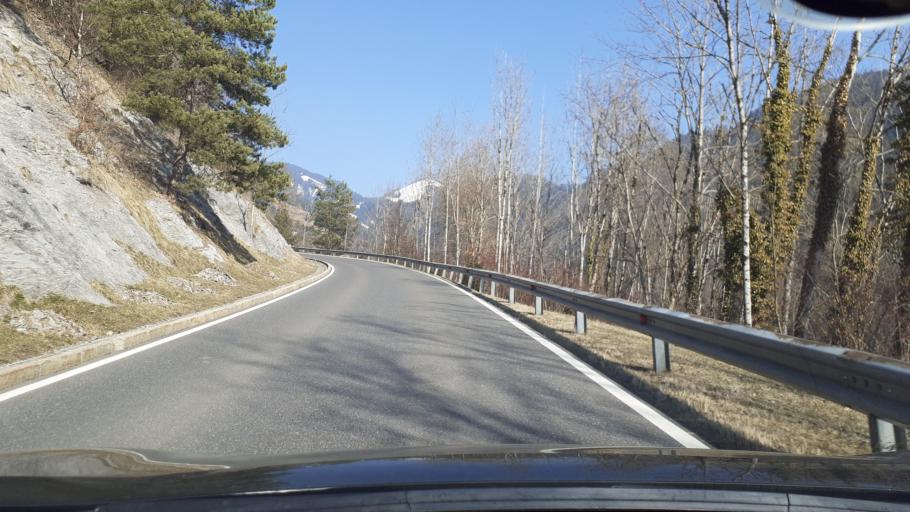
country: AT
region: Vorarlberg
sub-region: Politischer Bezirk Feldkirch
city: Fraxern
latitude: 47.3097
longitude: 9.6695
